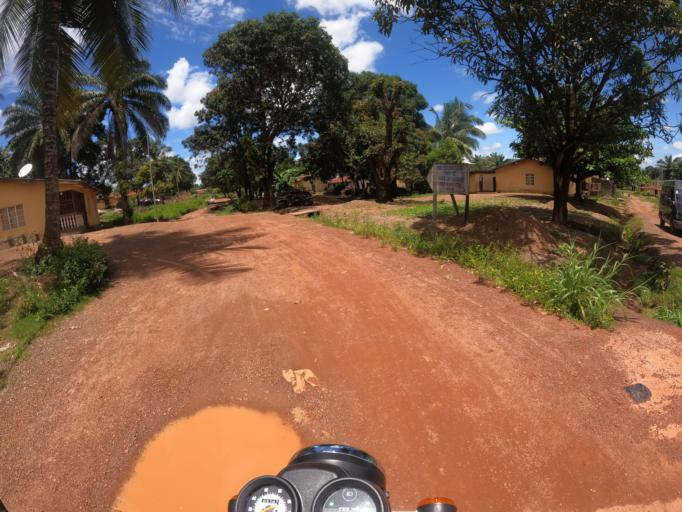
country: SL
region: Northern Province
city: Makeni
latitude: 8.8938
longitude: -12.0605
